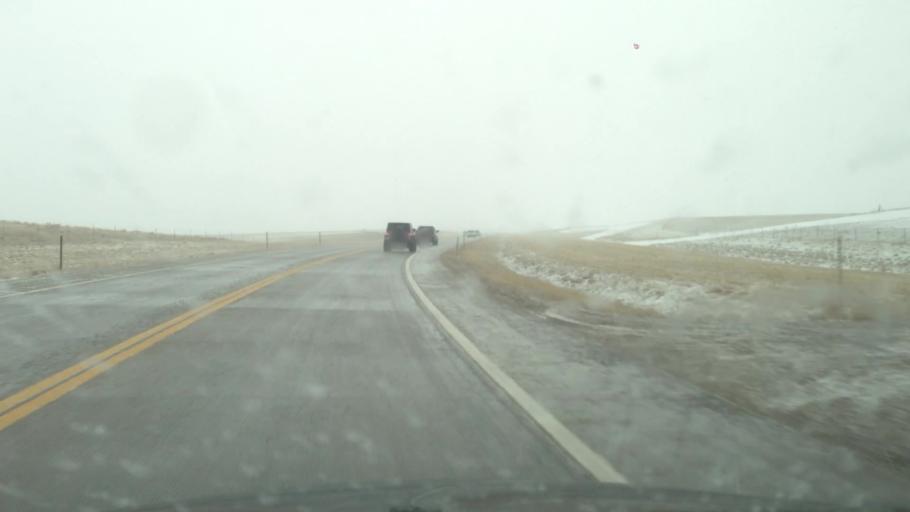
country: US
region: Colorado
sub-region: Park County
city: Castle Pines North
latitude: 39.4861
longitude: -104.8521
